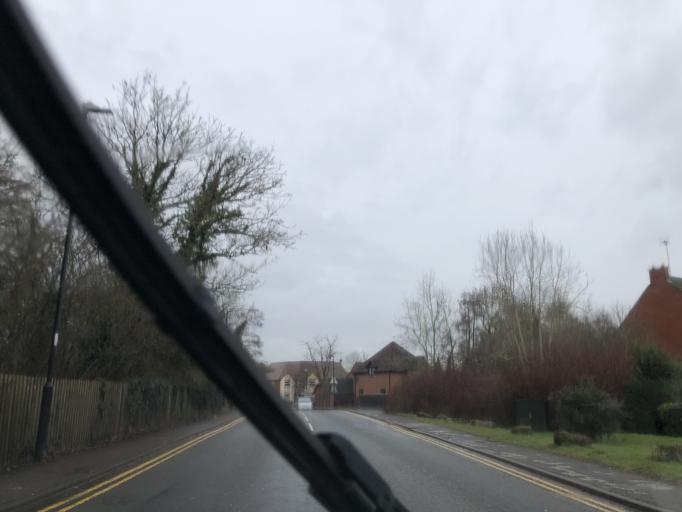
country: GB
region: England
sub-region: Warwickshire
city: Henley in Arden
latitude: 52.2869
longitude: -1.7756
